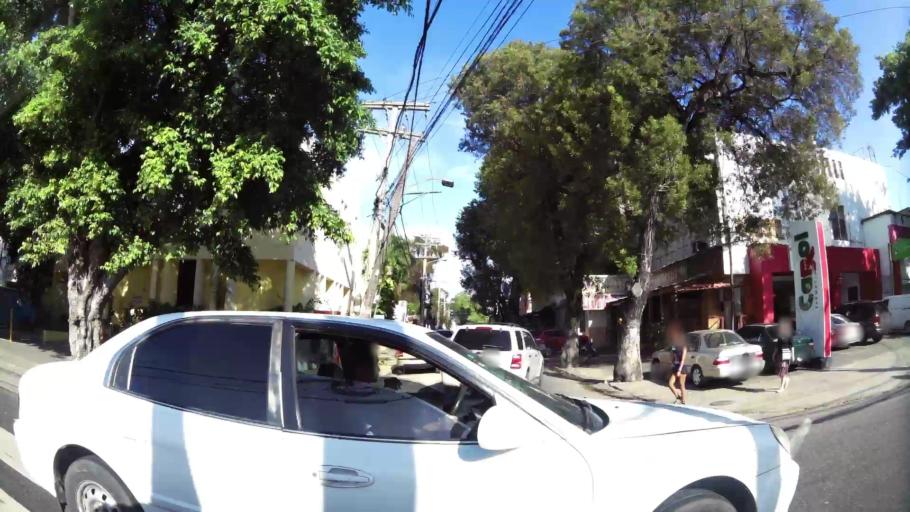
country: DO
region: Nacional
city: Ciudad Nueva
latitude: 18.4686
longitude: -69.8942
